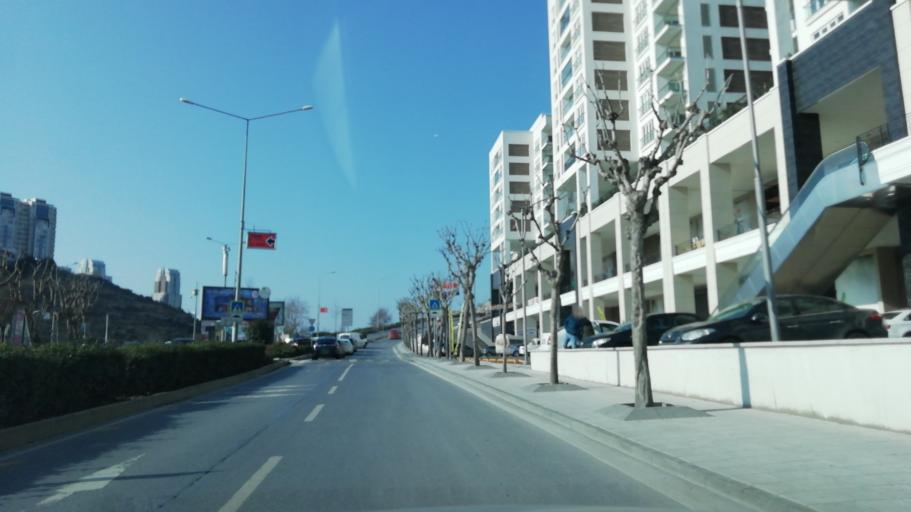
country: TR
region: Istanbul
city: Esenyurt
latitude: 41.0725
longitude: 28.6932
